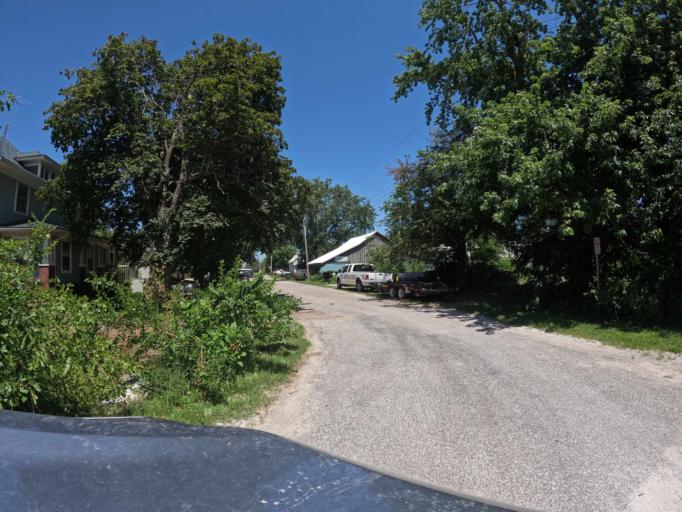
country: US
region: Iowa
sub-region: Keokuk County
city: Sigourney
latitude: 41.4536
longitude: -92.3346
